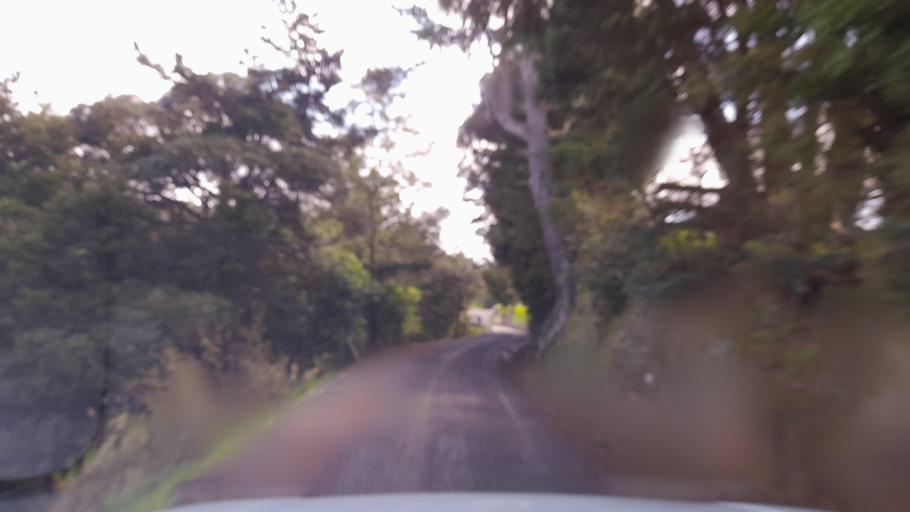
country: NZ
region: Northland
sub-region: Far North District
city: Waimate North
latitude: -35.1533
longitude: 173.7151
